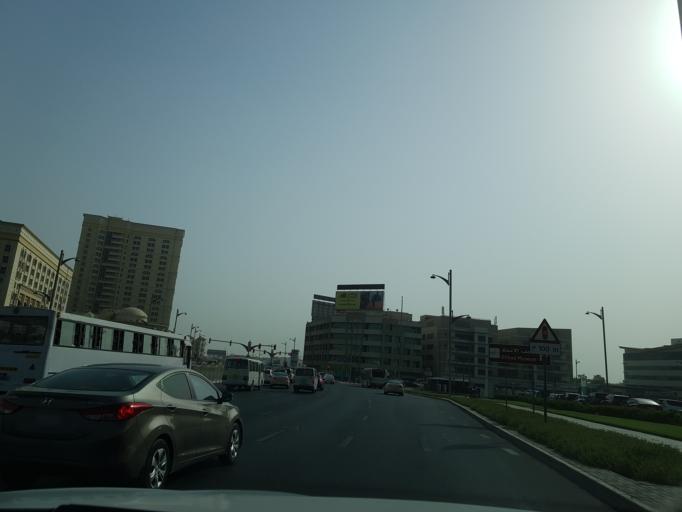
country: AE
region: Ash Shariqah
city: Sharjah
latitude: 25.2400
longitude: 55.2735
